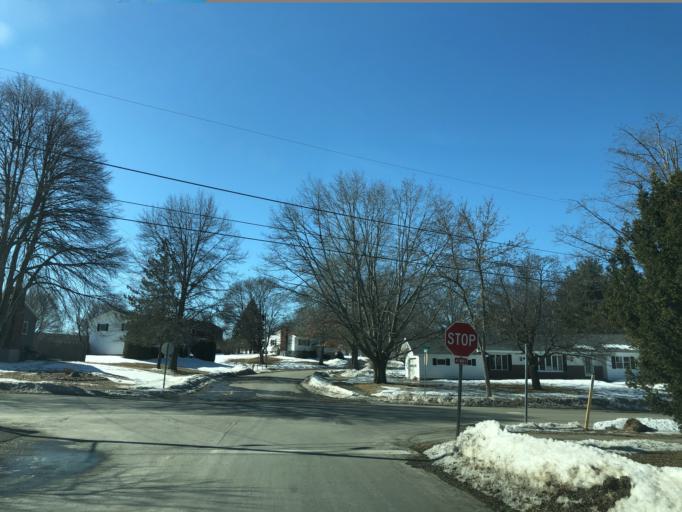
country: US
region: Maine
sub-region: Penobscot County
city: Brewer
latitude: 44.8183
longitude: -68.7566
